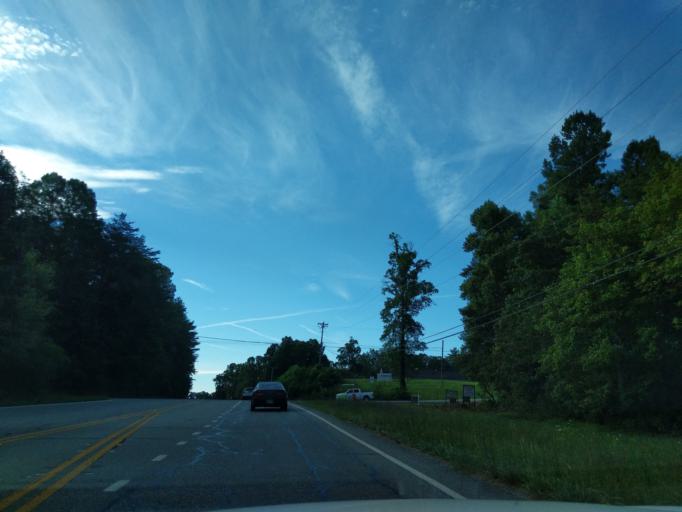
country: US
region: Georgia
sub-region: Fannin County
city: Blue Ridge
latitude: 34.9043
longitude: -84.3743
